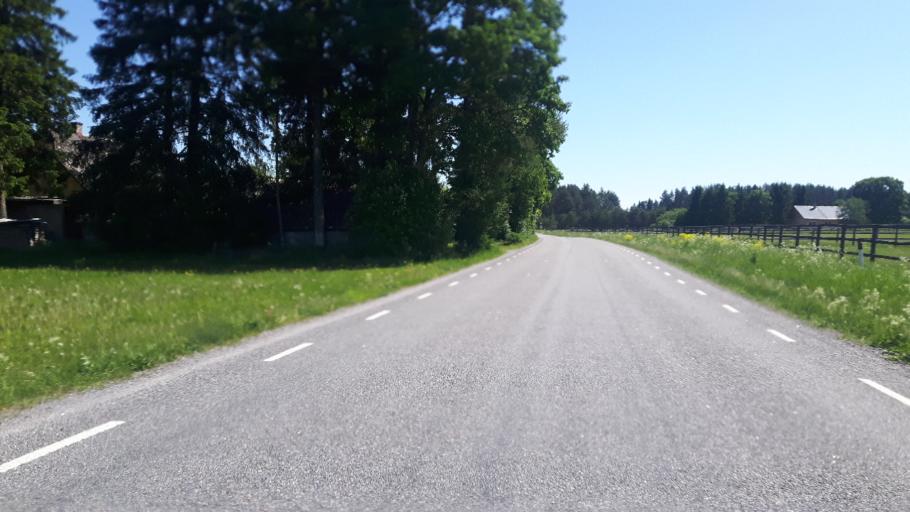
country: EE
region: Raplamaa
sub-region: Kohila vald
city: Kohila
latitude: 59.1956
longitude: 24.6984
